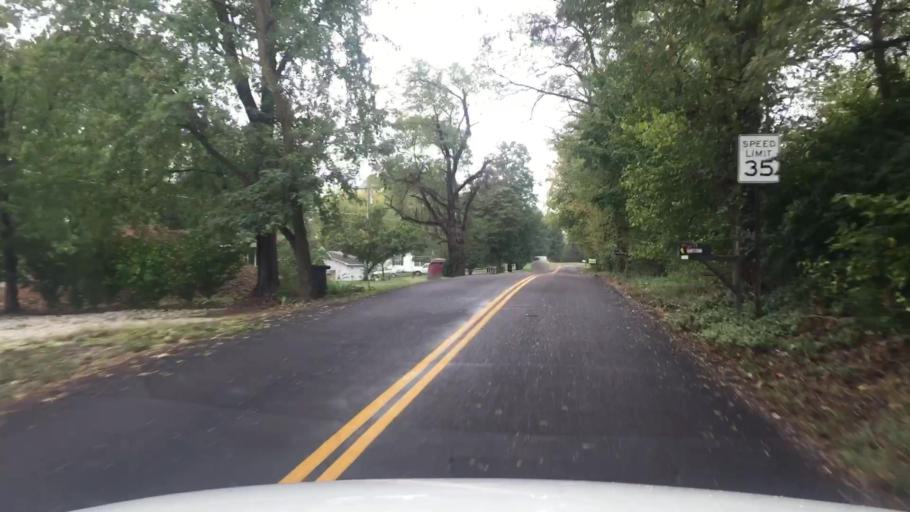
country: US
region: Missouri
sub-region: Boone County
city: Columbia
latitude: 38.8607
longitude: -92.3327
